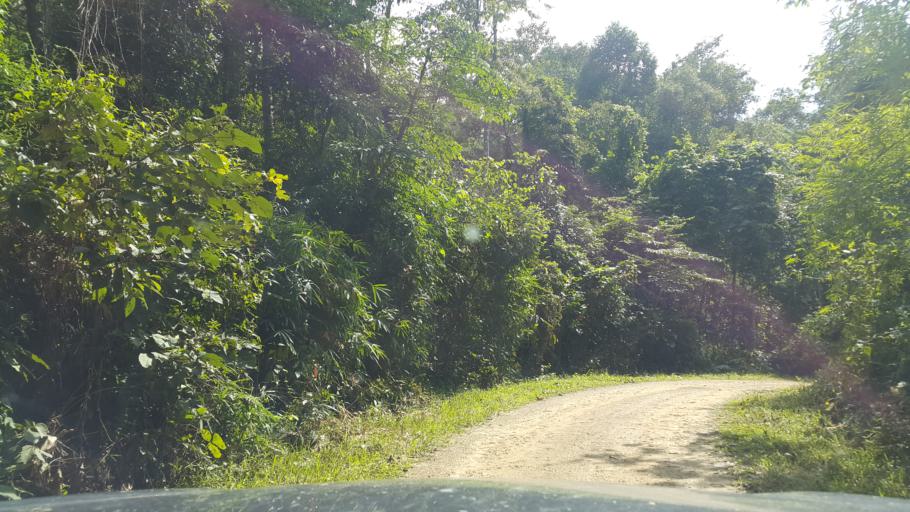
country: TH
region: Chiang Mai
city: Phrao
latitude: 19.0909
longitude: 99.2582
